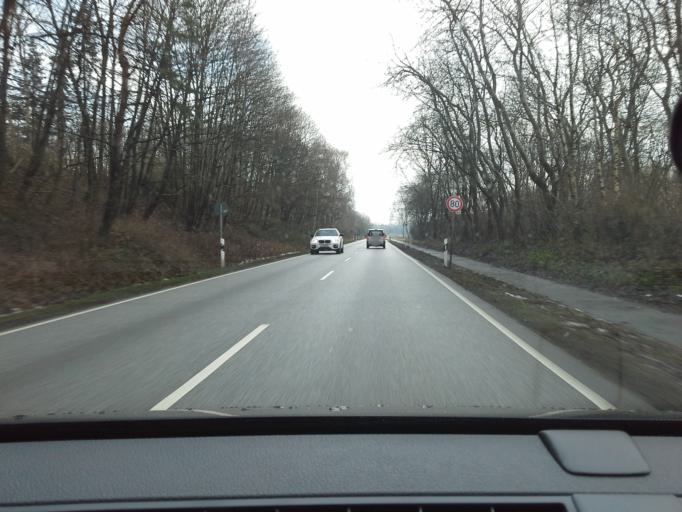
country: DE
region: Schleswig-Holstein
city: Ellerau
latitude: 53.7419
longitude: 9.9569
